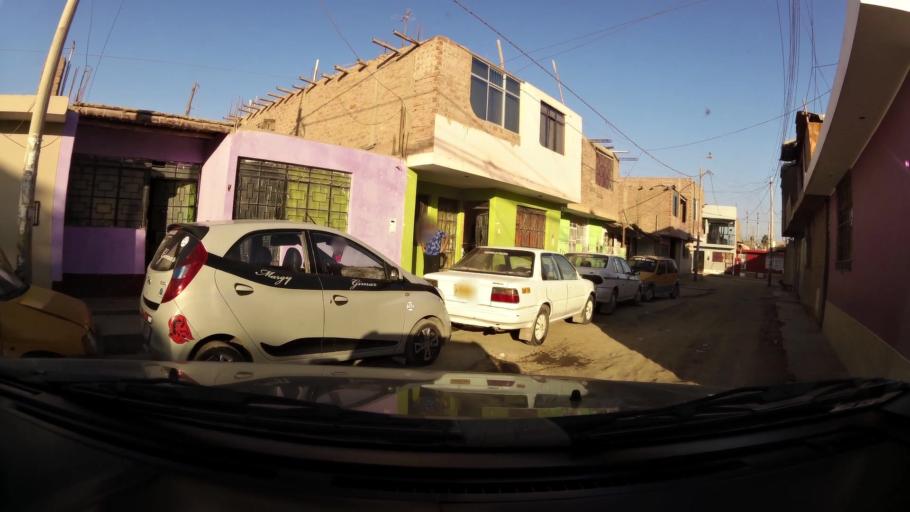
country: PE
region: Ica
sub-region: Provincia de Ica
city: Ica
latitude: -14.0567
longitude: -75.7274
